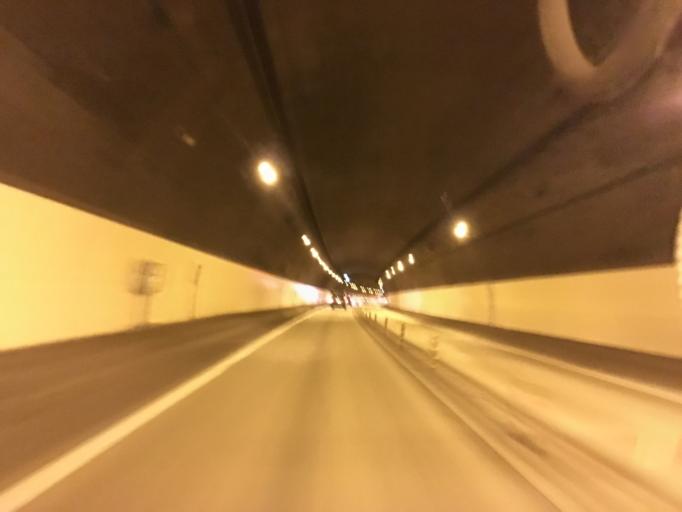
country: JP
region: Miyagi
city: Wakuya
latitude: 38.6322
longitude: 141.2791
